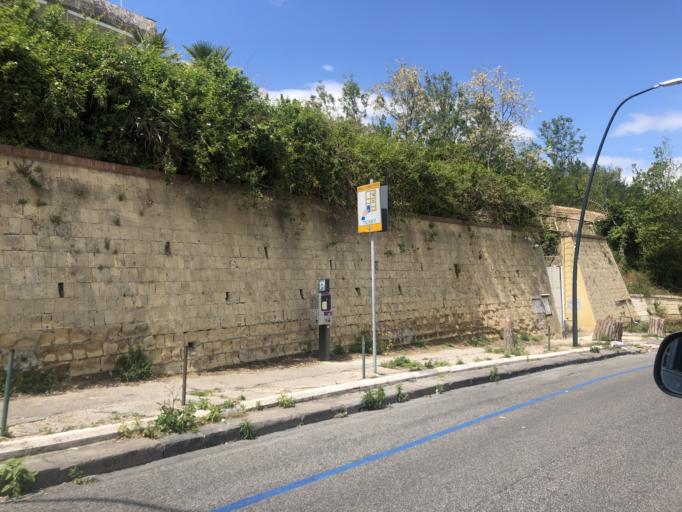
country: IT
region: Campania
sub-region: Provincia di Napoli
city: Bagnoli
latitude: 40.7989
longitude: 14.1831
